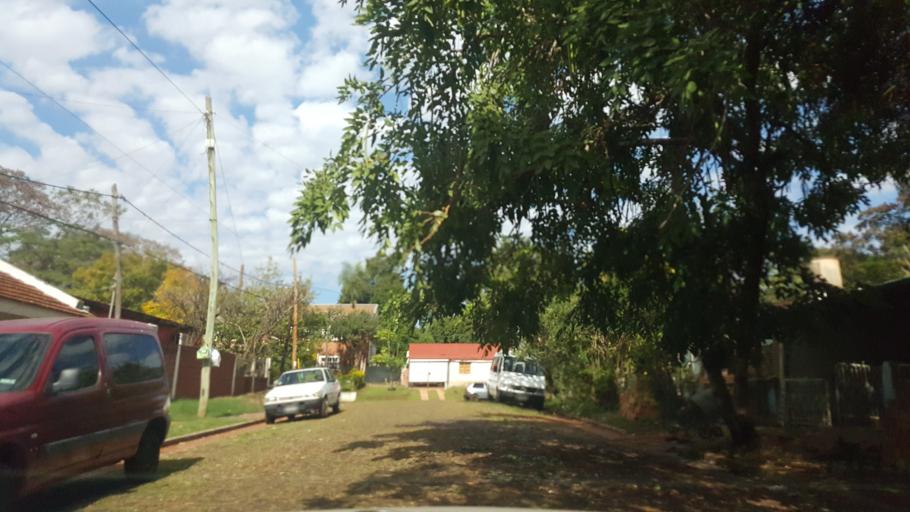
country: AR
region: Misiones
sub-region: Departamento de Capital
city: Posadas
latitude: -27.3666
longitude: -55.9229
